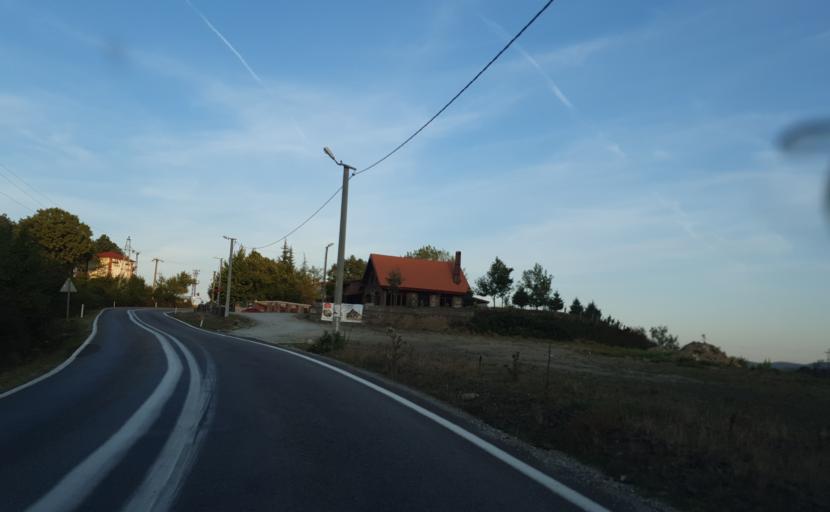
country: TR
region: Kirklareli
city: Sergen
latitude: 41.8214
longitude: 27.7555
